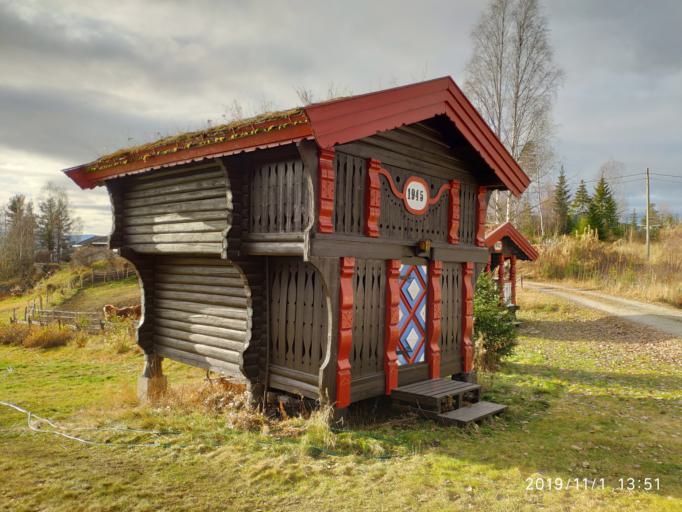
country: NO
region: Buskerud
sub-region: Gol
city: Gol
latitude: 60.7161
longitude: 8.9481
